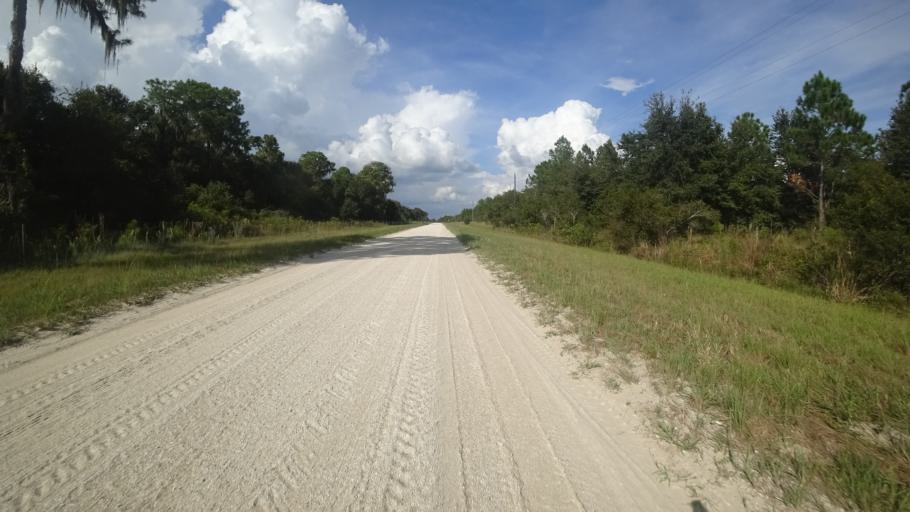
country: US
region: Florida
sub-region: Hillsborough County
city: Balm
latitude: 27.6087
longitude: -82.1197
